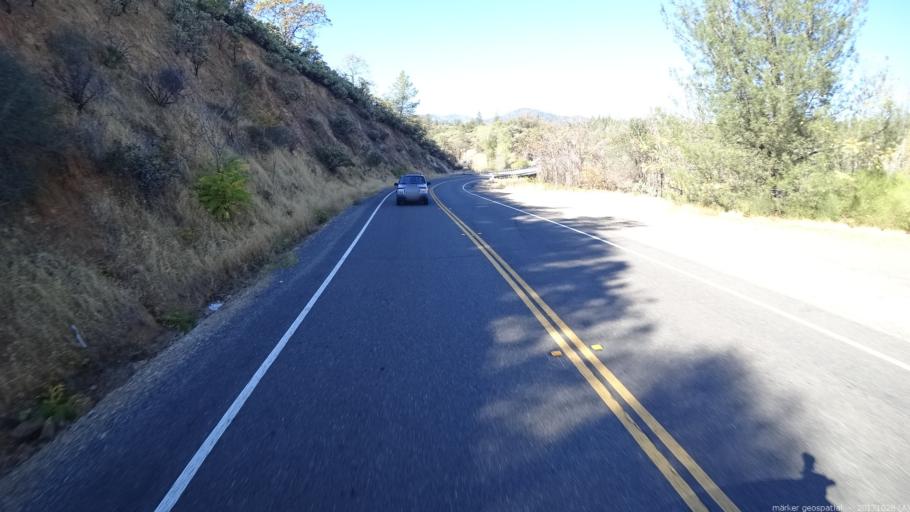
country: US
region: California
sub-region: Shasta County
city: Shasta
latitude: 40.6126
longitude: -122.4594
